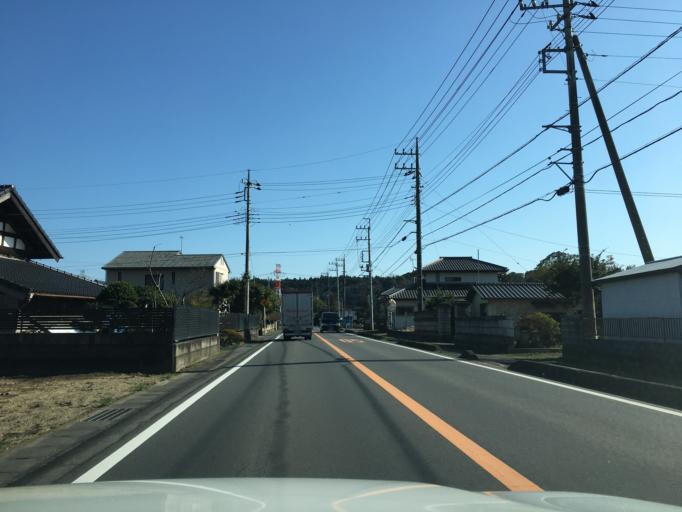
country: JP
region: Ibaraki
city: Omiya
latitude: 36.4927
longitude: 140.3746
